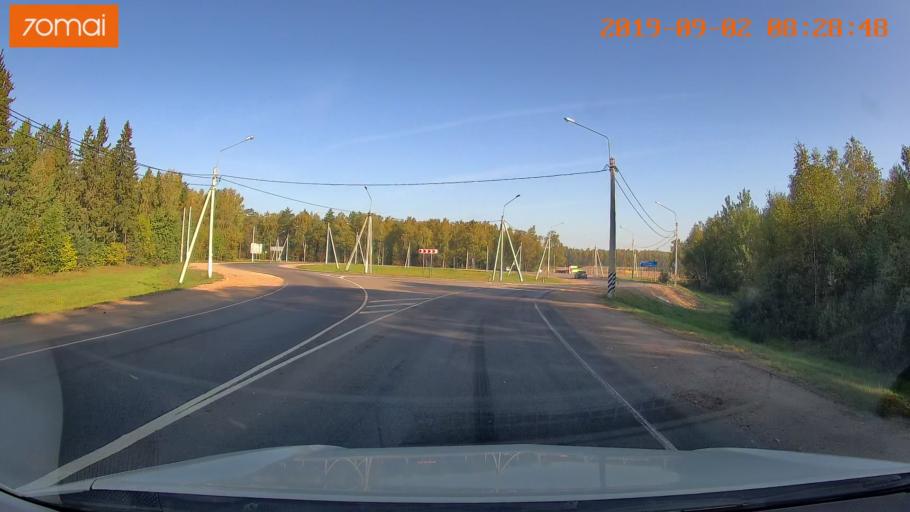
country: RU
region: Kaluga
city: Maloyaroslavets
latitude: 54.9990
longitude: 36.3960
